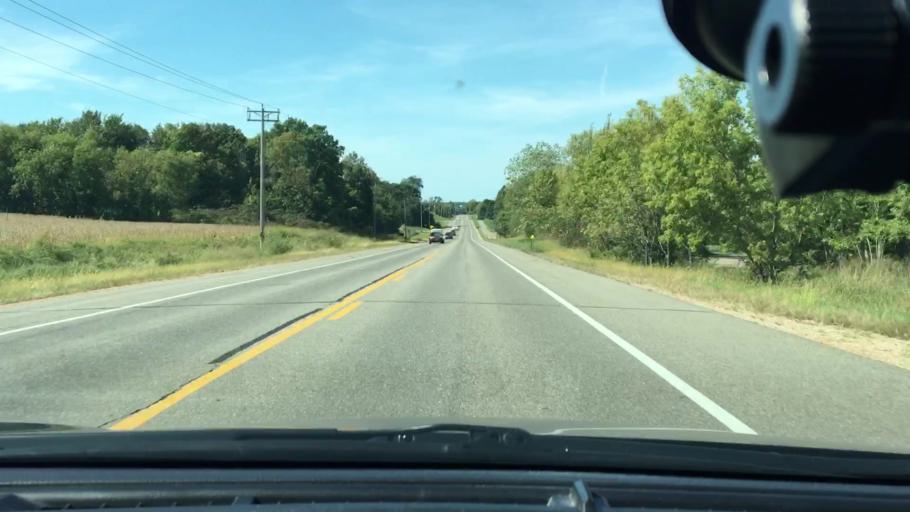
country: US
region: Minnesota
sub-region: Wright County
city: Hanover
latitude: 45.1526
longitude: -93.6420
